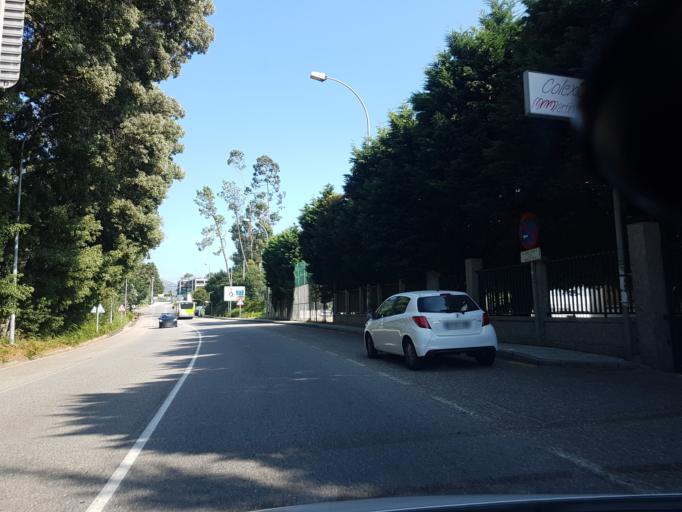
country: ES
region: Galicia
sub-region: Provincia de Pontevedra
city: Redondela
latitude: 42.2293
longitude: -8.6355
